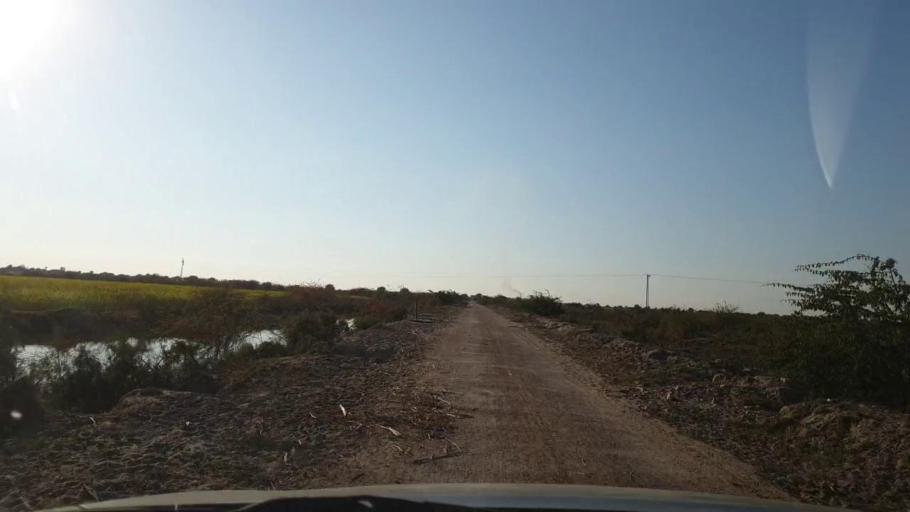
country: PK
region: Sindh
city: Jhol
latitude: 25.8980
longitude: 68.9380
